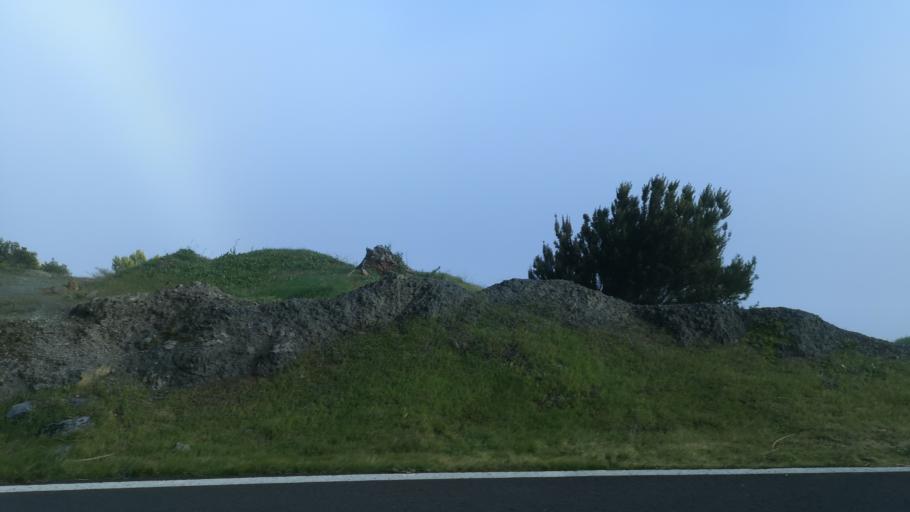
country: ES
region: Canary Islands
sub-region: Provincia de Santa Cruz de Tenerife
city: Alajero
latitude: 28.1009
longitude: -17.2464
